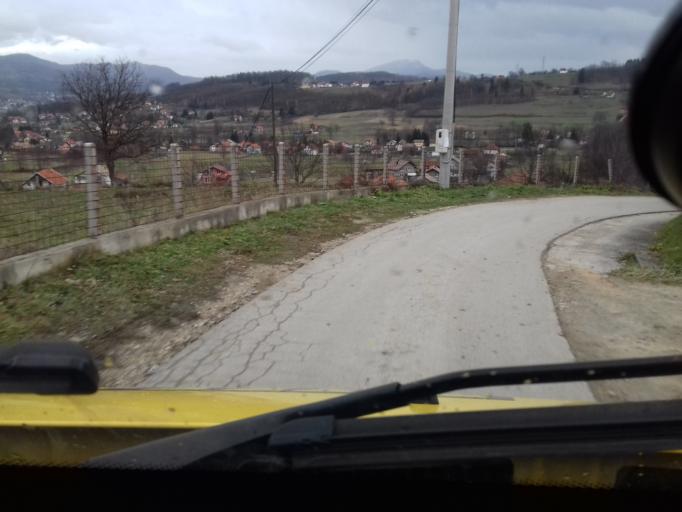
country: BA
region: Federation of Bosnia and Herzegovina
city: Vitez
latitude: 44.1364
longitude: 17.7874
